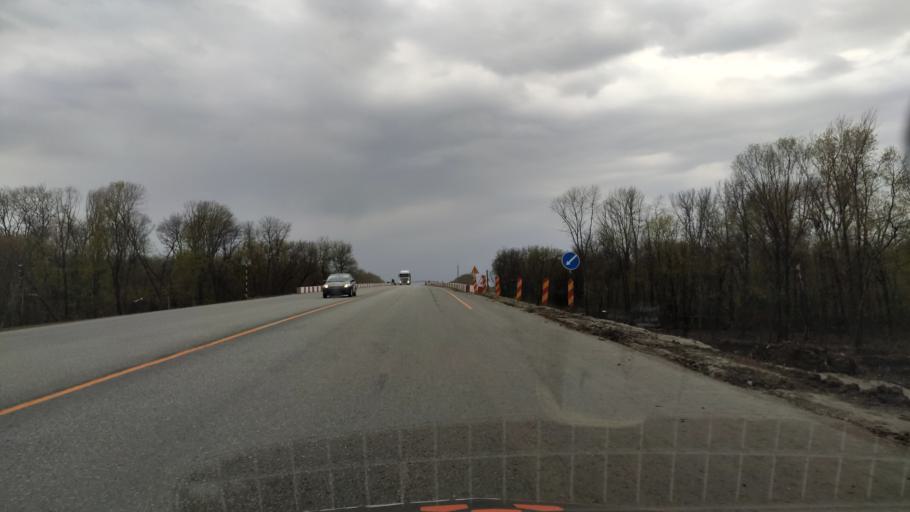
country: RU
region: Kursk
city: Gorshechnoye
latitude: 51.5511
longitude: 38.0418
